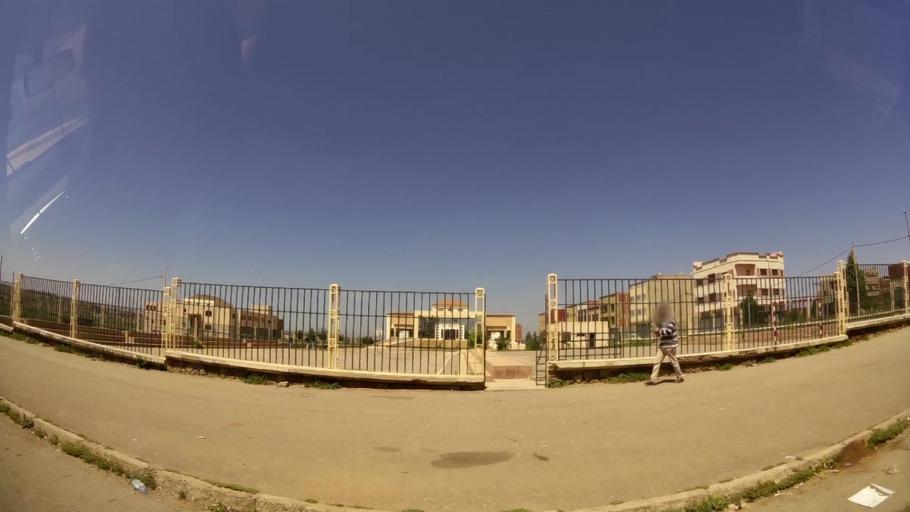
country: MA
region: Oriental
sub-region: Oujda-Angad
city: Oujda
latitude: 34.6900
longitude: -1.9313
